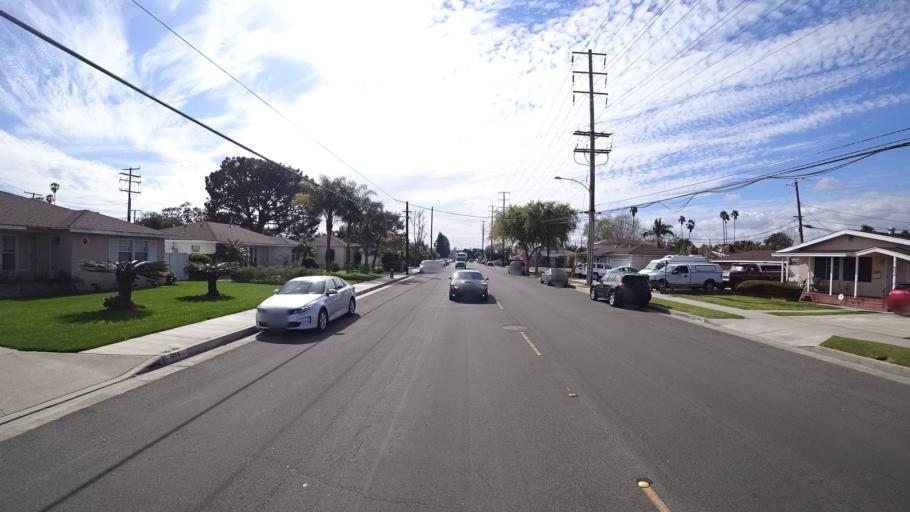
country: US
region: California
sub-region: Orange County
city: Anaheim
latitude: 33.8418
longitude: -117.9277
